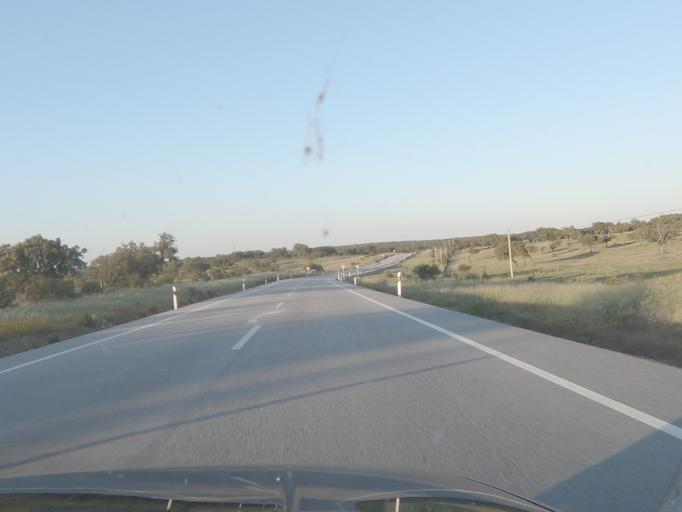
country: ES
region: Extremadura
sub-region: Provincia de Caceres
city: Carbajo
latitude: 39.5023
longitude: -7.1693
